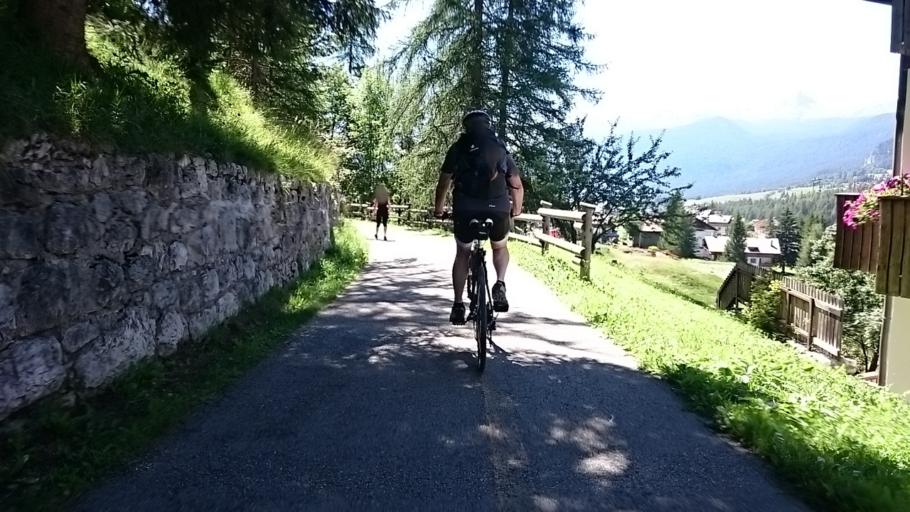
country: IT
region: Veneto
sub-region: Provincia di Belluno
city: Cortina d'Ampezzo
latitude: 46.5546
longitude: 12.1295
